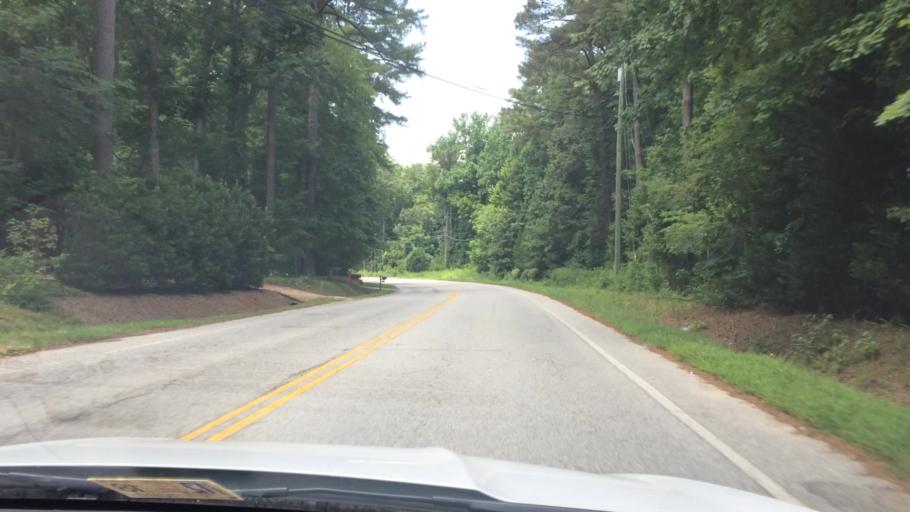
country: US
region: Virginia
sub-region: York County
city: Yorktown
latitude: 37.2025
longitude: -76.4885
